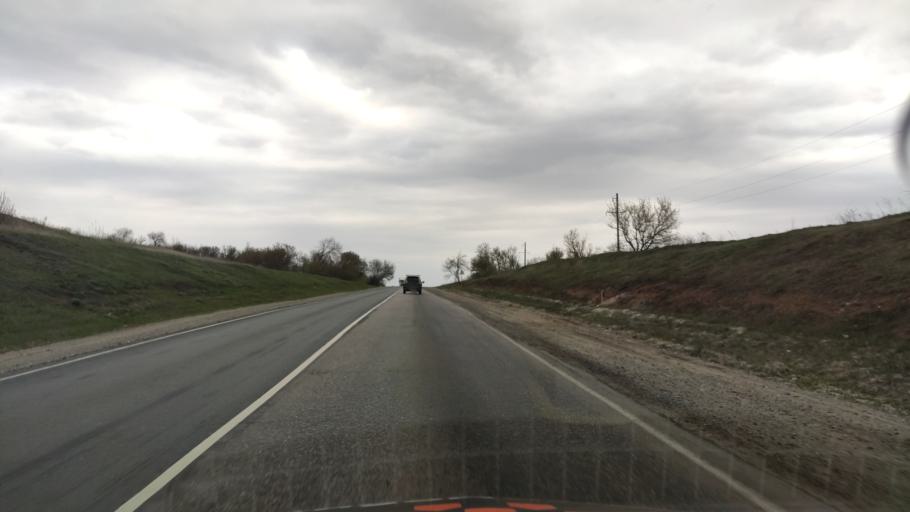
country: RU
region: Voronezj
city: Nizhnedevitsk
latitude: 51.5642
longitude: 38.3821
